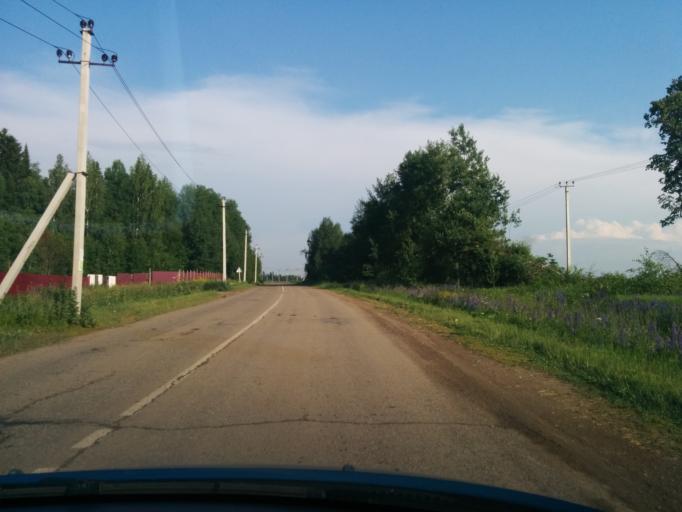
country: RU
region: Perm
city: Polazna
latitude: 58.2419
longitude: 56.2674
